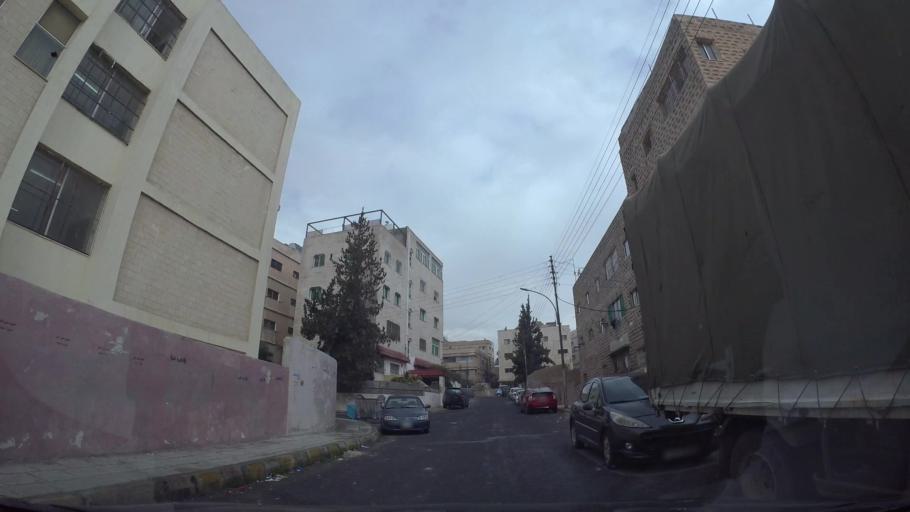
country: JO
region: Amman
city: Amman
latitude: 31.9604
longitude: 35.9393
